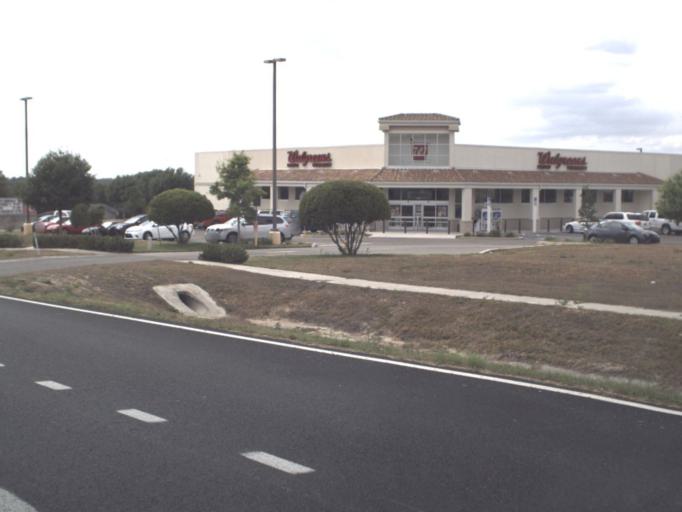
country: US
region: Florida
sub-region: Lake County
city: Groveland
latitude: 28.5581
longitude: -81.8233
